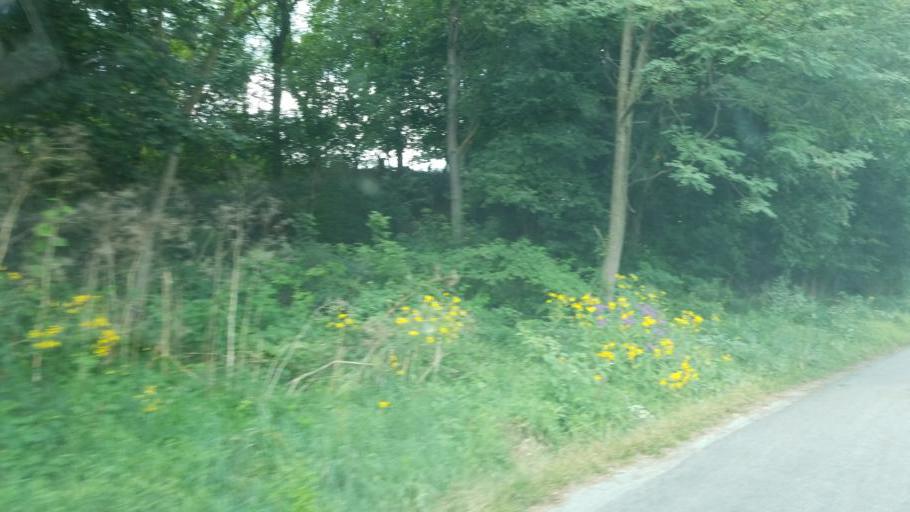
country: US
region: Ohio
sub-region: Knox County
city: Oak Hill
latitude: 40.4009
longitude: -82.2801
